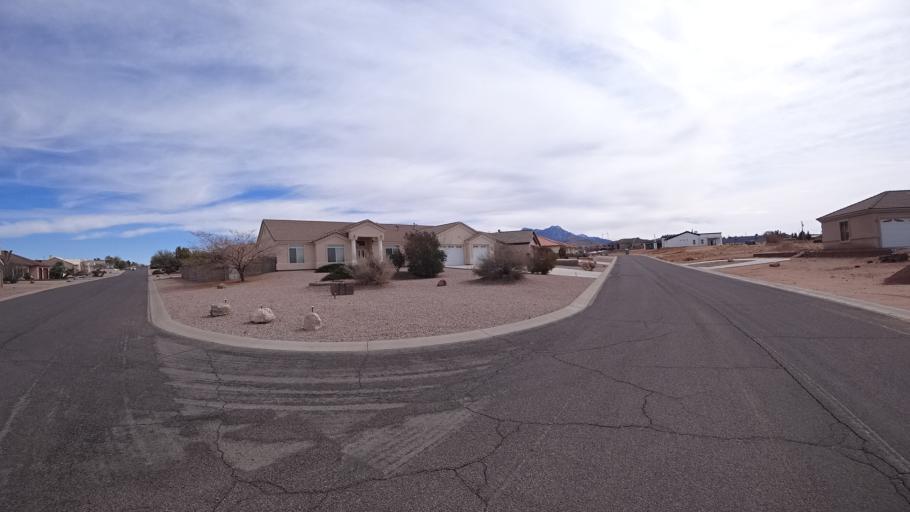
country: US
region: Arizona
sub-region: Mohave County
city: Kingman
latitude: 35.1952
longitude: -113.9845
